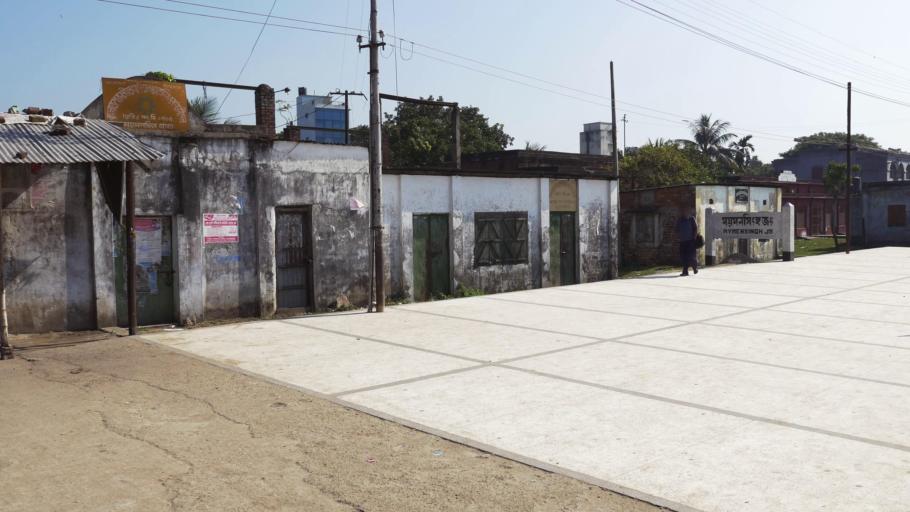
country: BD
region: Dhaka
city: Mymensingh
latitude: 24.6572
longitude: 90.4542
